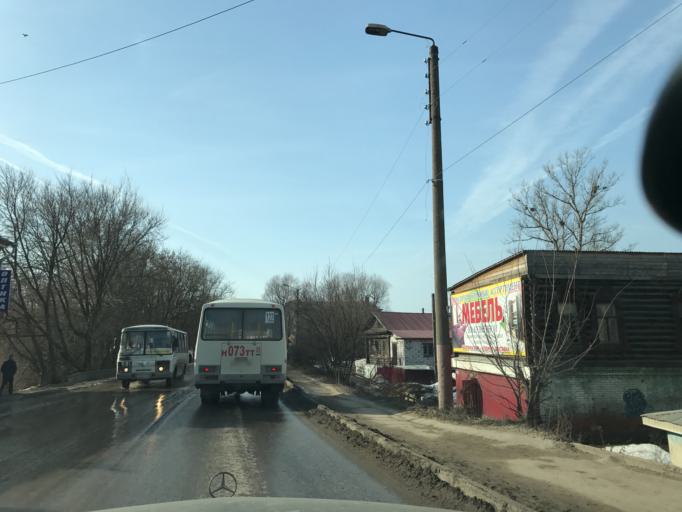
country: RU
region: Nizjnij Novgorod
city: Pavlovo
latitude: 55.9669
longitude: 43.0711
